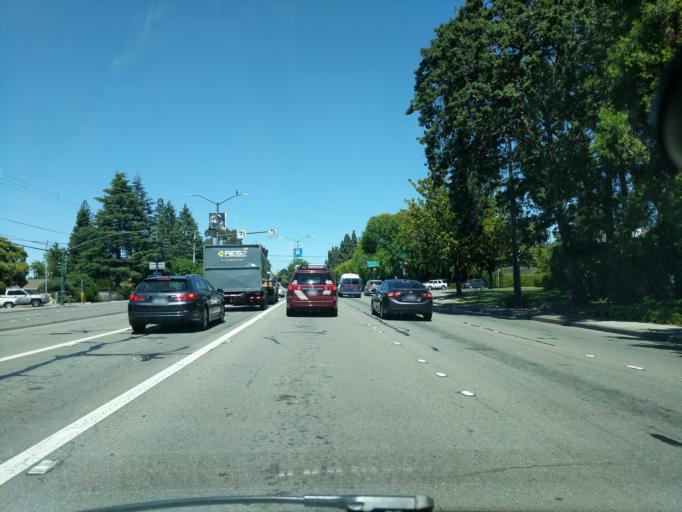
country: US
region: California
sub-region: Contra Costa County
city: Waldon
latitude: 37.9205
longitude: -122.0350
